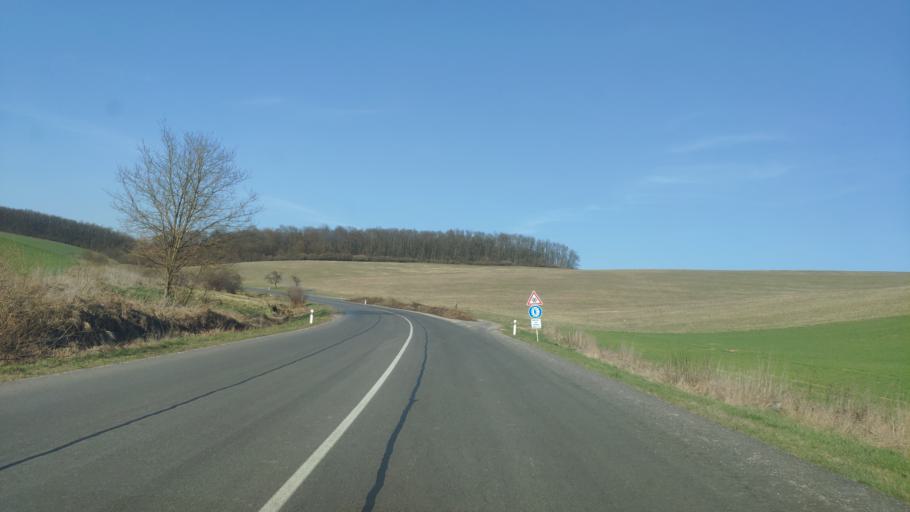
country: HU
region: Borsod-Abauj-Zemplen
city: Putnok
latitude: 48.4903
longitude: 20.2789
